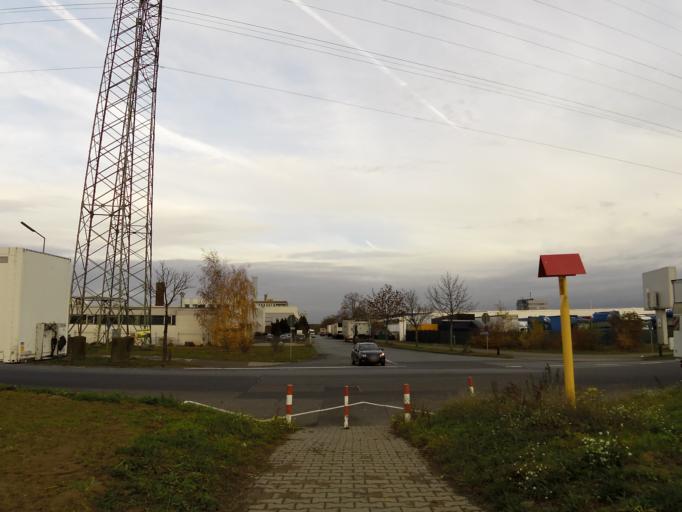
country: DE
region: Hesse
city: Morfelden-Walldorf
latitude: 49.9828
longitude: 8.5790
